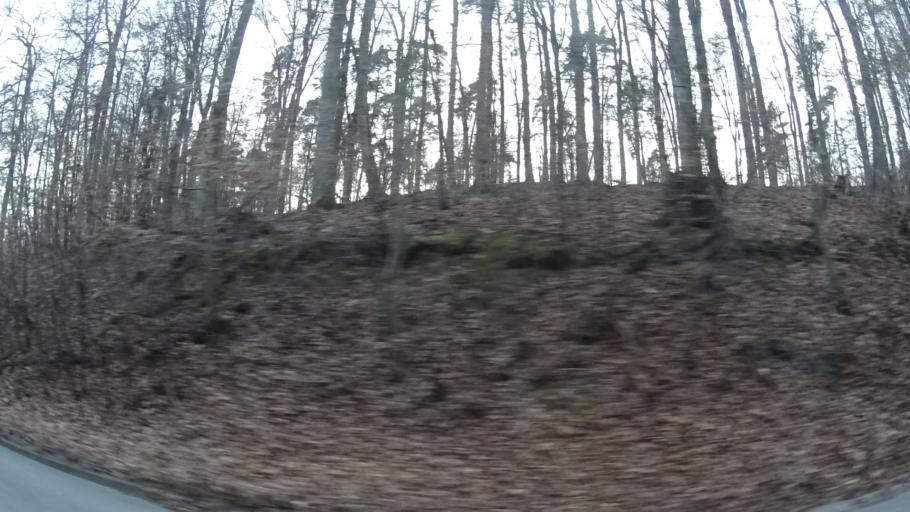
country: DE
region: Baden-Wuerttemberg
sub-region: Regierungsbezirk Stuttgart
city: Gerlingen
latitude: 48.7791
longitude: 9.0638
